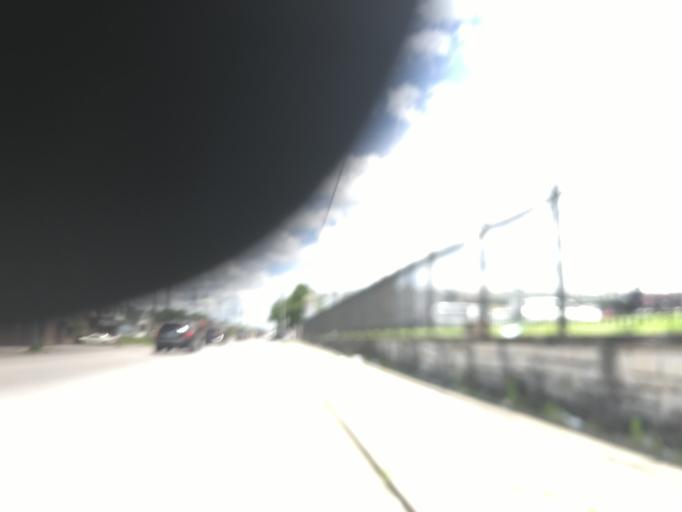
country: US
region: Kentucky
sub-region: Jefferson County
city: Louisville
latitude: 38.2494
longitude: -85.7972
